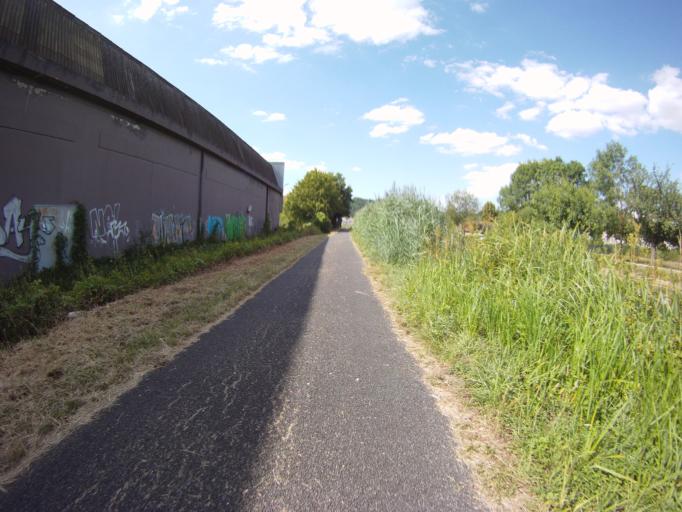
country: FR
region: Lorraine
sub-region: Departement de la Meuse
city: Bar-le-Duc
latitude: 48.7673
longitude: 5.1776
